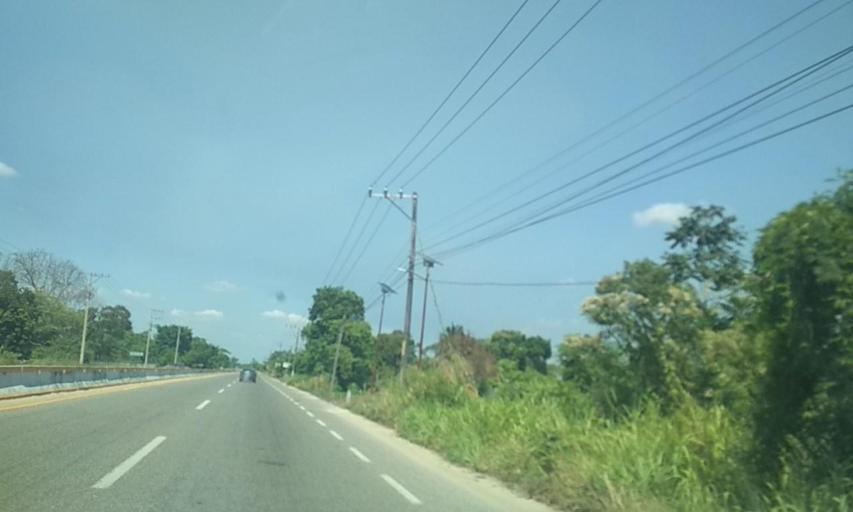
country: MX
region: Tabasco
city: Huimanguillo
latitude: 17.8607
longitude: -93.3903
